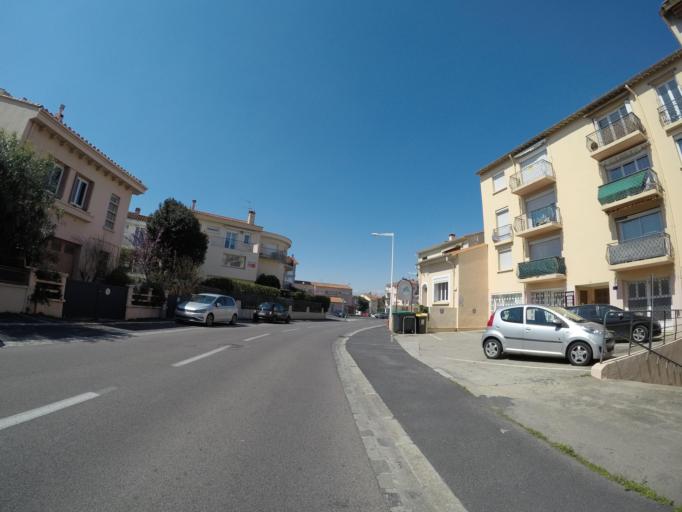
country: FR
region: Languedoc-Roussillon
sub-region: Departement des Pyrenees-Orientales
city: Perpignan
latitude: 42.6959
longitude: 2.9091
